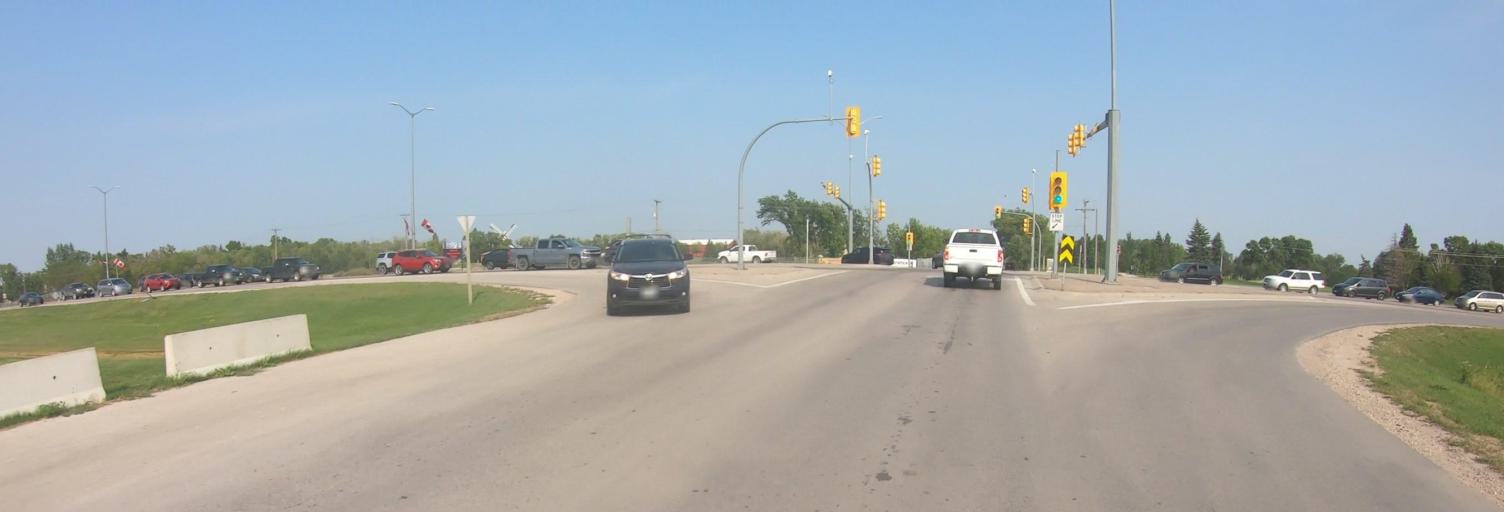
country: CA
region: Manitoba
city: Steinbach
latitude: 49.5484
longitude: -96.6890
